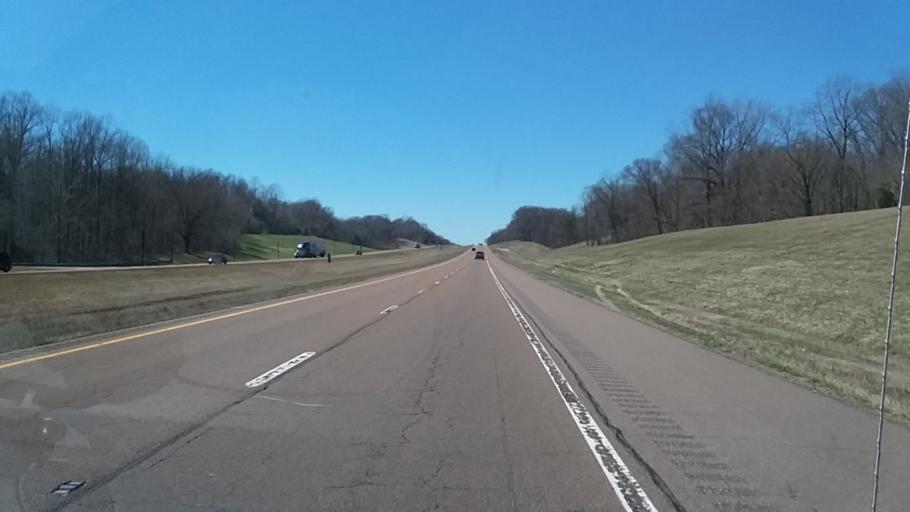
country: US
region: Tennessee
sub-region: Dyer County
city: Dyersburg
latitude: 36.0729
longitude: -89.4726
